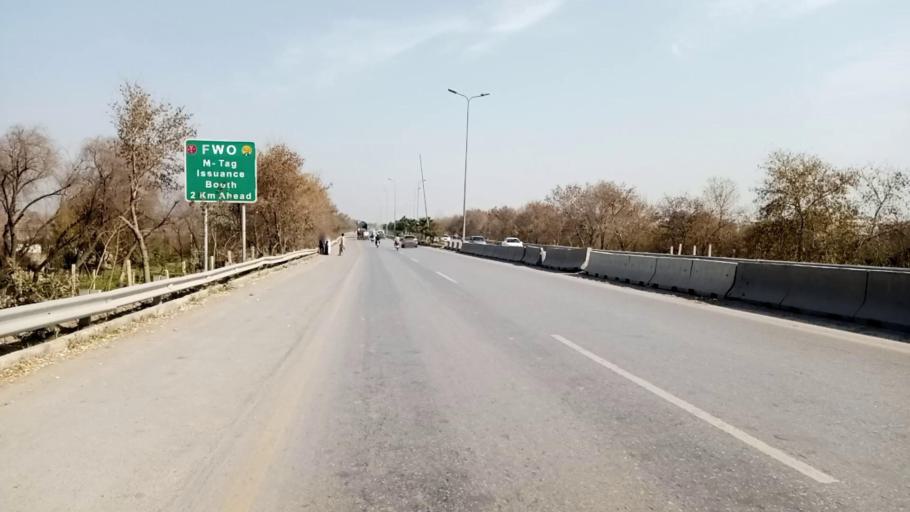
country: PK
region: Khyber Pakhtunkhwa
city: Peshawar
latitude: 34.0253
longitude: 71.6321
